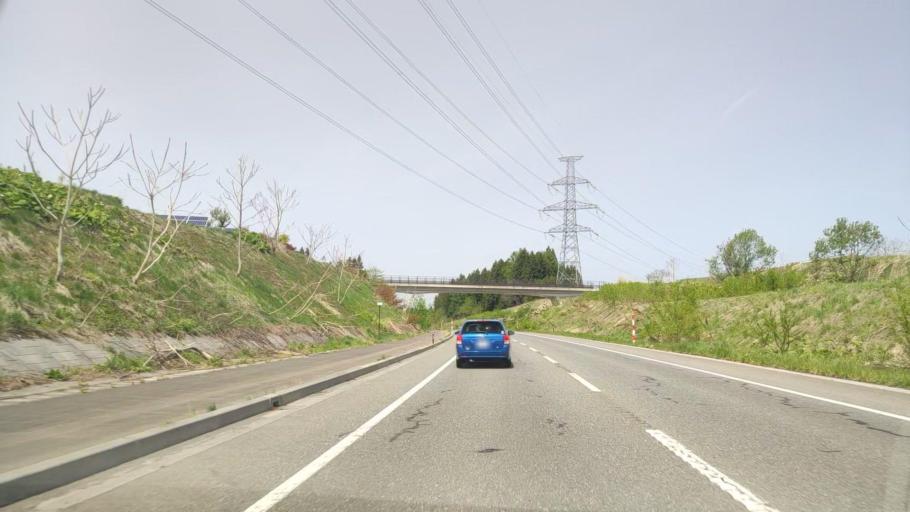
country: JP
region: Aomori
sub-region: Misawa Shi
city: Inuotose
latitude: 40.6840
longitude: 141.1704
